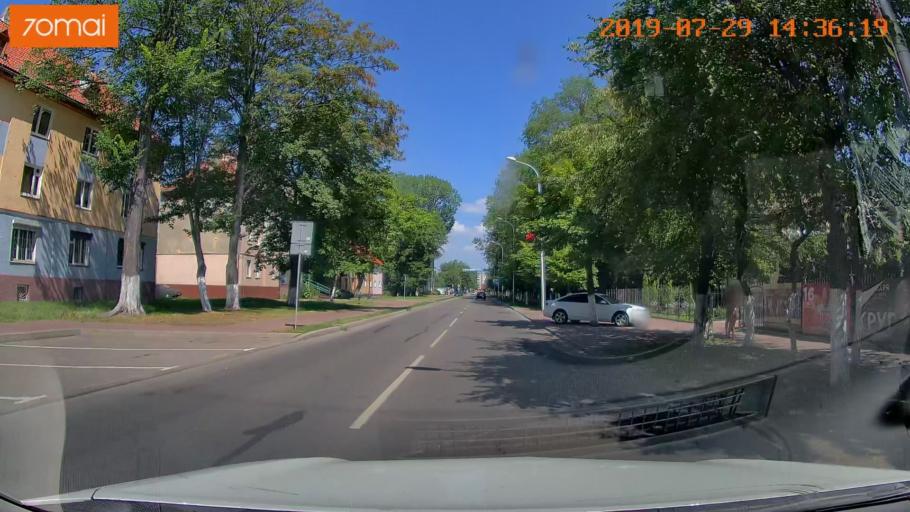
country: RU
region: Kaliningrad
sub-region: Gorod Kaliningrad
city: Baltiysk
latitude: 54.6464
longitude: 19.8990
